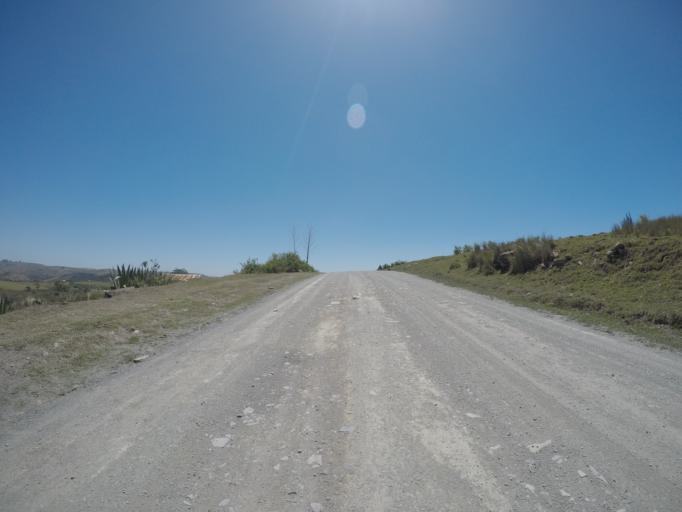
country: ZA
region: Eastern Cape
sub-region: OR Tambo District Municipality
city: Libode
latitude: -32.0095
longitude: 29.0734
